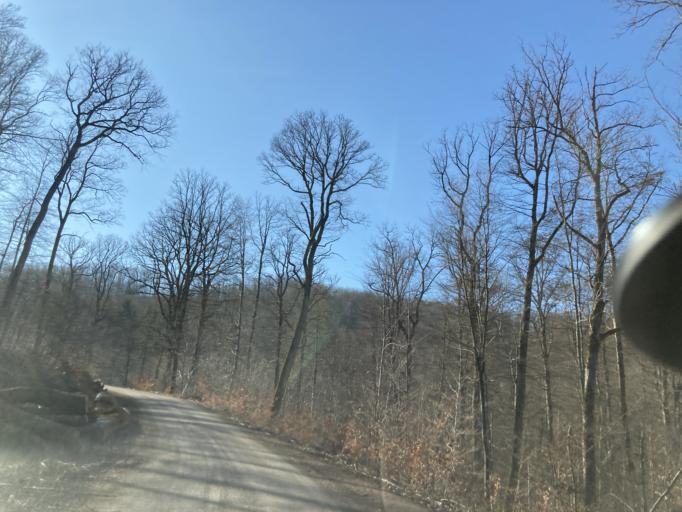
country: DE
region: Baden-Wuerttemberg
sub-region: Tuebingen Region
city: Mossingen
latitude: 48.3742
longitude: 9.0292
